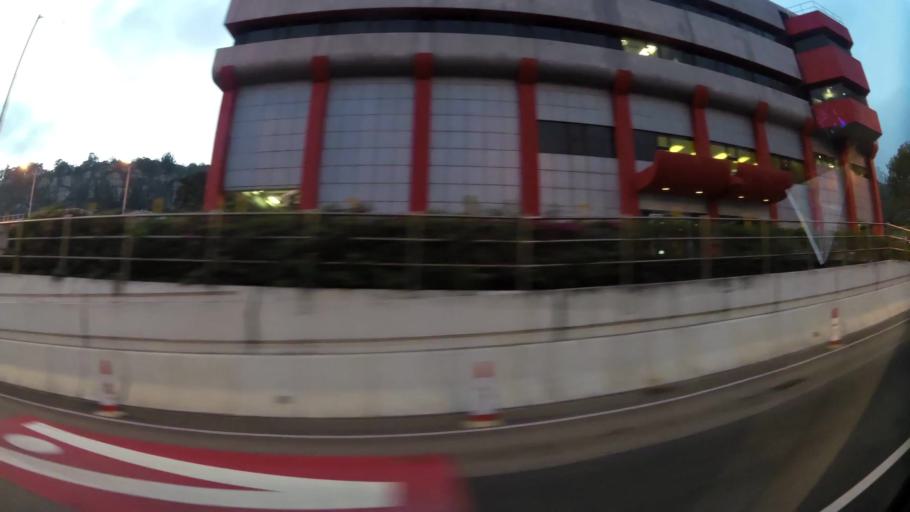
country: HK
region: Kowloon City
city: Kowloon
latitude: 22.3003
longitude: 114.2321
